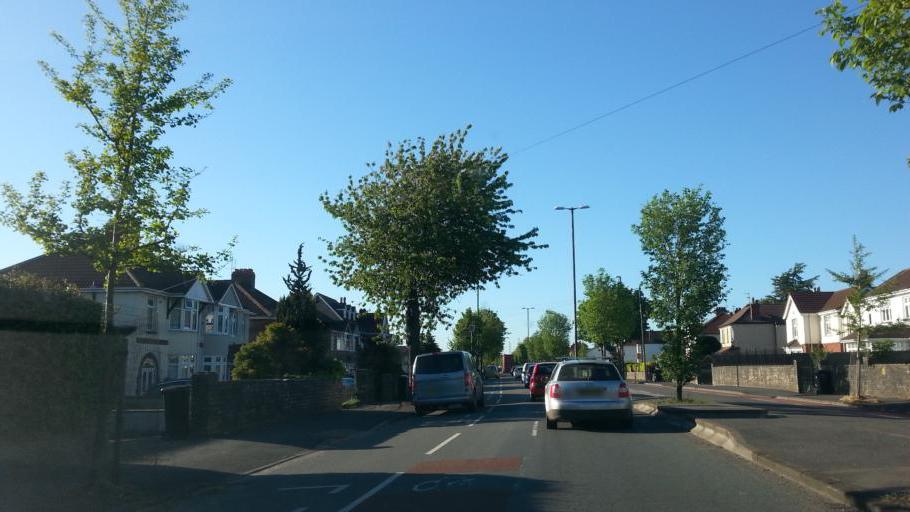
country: GB
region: England
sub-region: Bath and North East Somerset
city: Whitchurch
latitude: 51.4187
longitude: -2.5606
